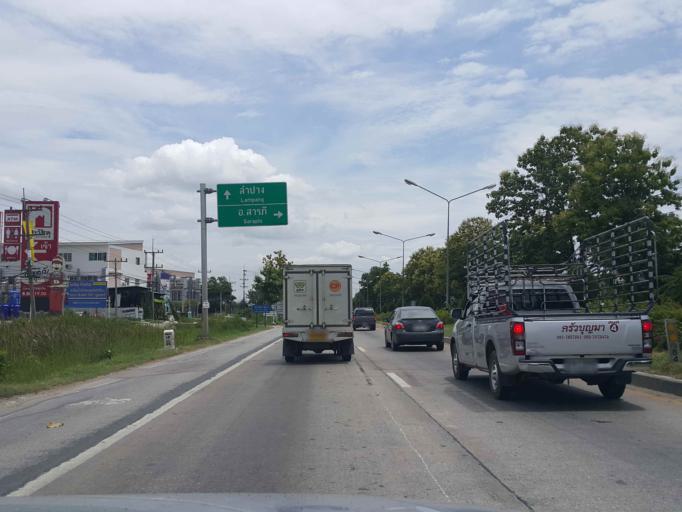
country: TH
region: Chiang Mai
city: Saraphi
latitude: 18.7209
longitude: 99.0421
